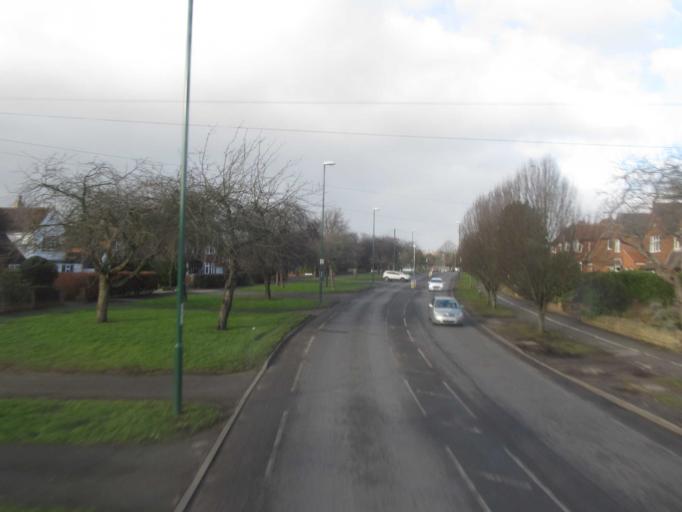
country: GB
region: England
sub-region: Nottinghamshire
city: Kimberley
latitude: 52.9430
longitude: -1.2236
